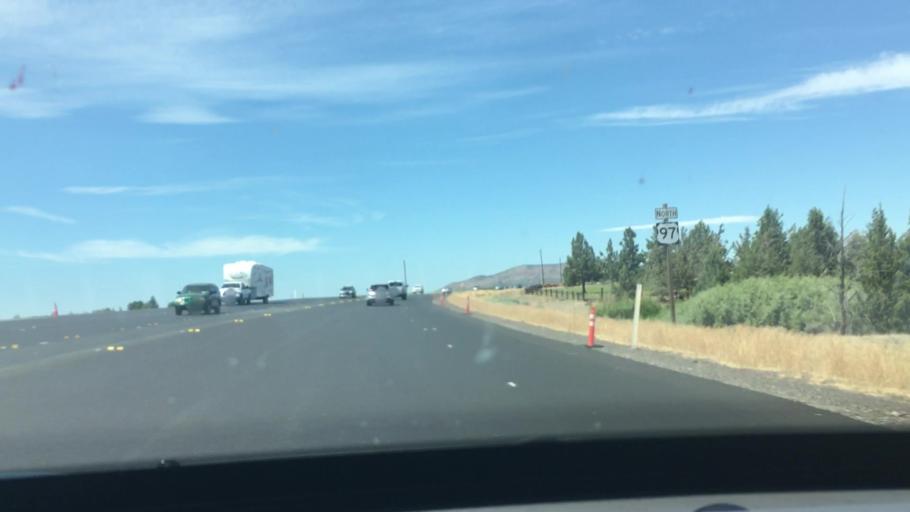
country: US
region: Oregon
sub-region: Deschutes County
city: Terrebonne
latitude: 44.3980
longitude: -121.1980
